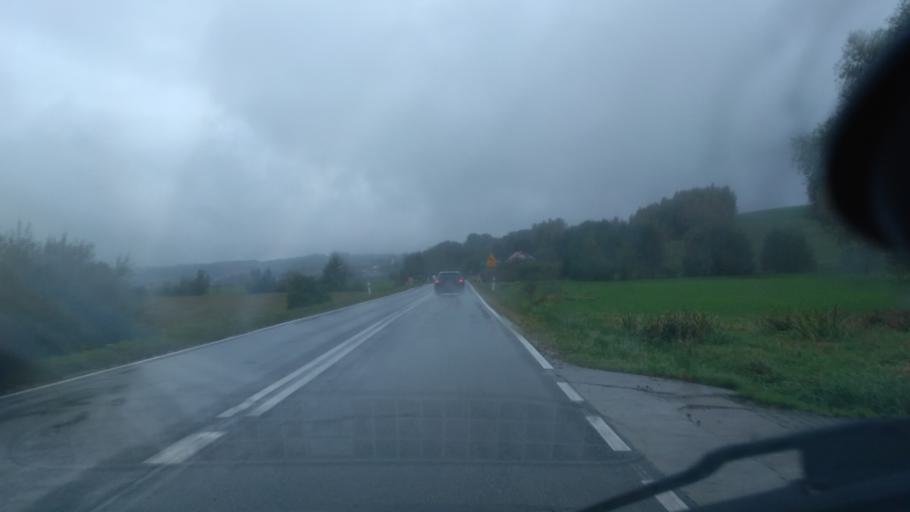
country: PL
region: Subcarpathian Voivodeship
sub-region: Powiat ropczycko-sedziszowski
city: Niedzwiada
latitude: 49.9825
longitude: 21.5596
